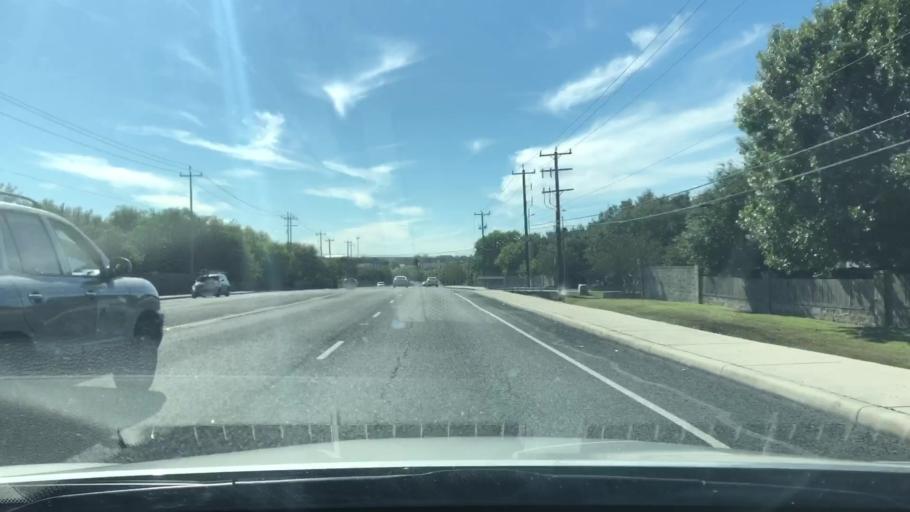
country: US
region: Texas
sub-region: Bexar County
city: Converse
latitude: 29.4888
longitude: -98.3399
